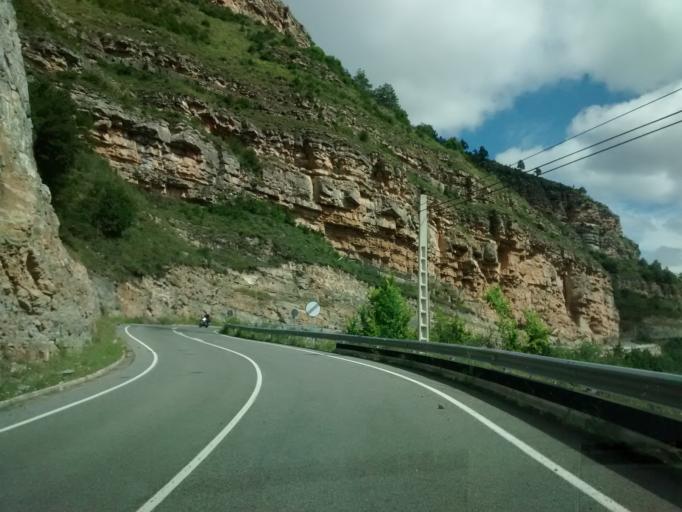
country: ES
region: La Rioja
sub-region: Provincia de La Rioja
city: Soto en Cameros
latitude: 42.2977
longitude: -2.4215
